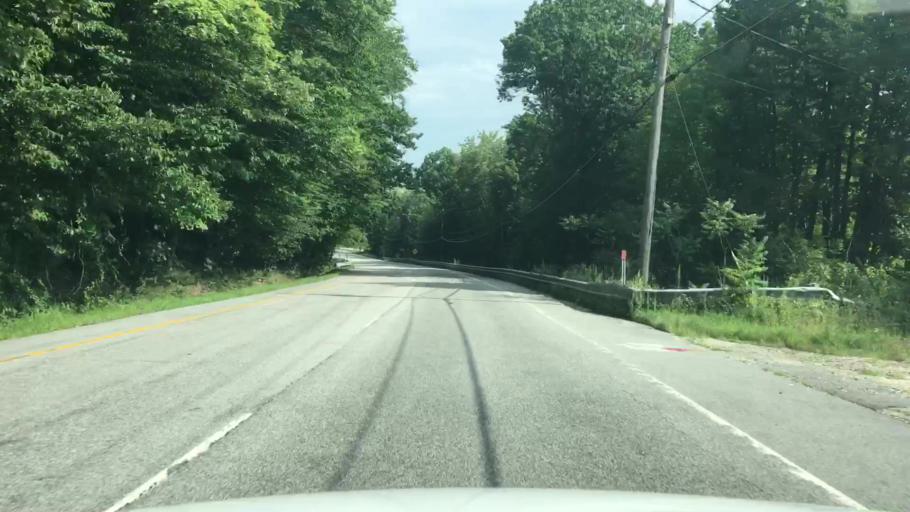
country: US
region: Maine
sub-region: Androscoggin County
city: Auburn
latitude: 44.0524
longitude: -70.2537
